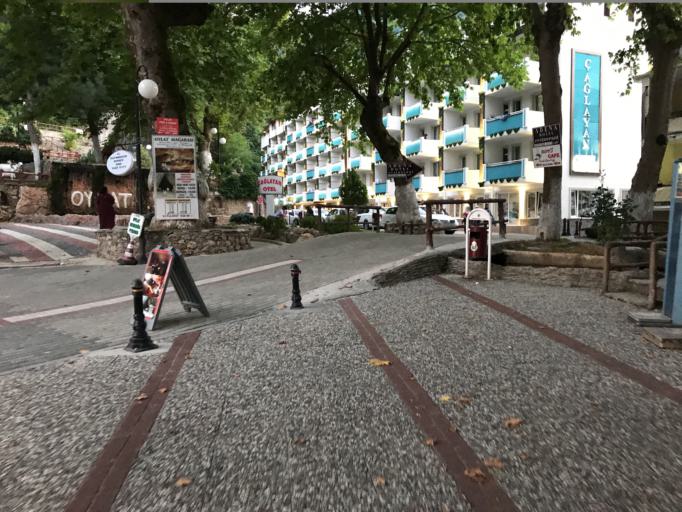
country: TR
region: Bursa
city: Tahtakopru
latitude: 39.9278
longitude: 29.5862
